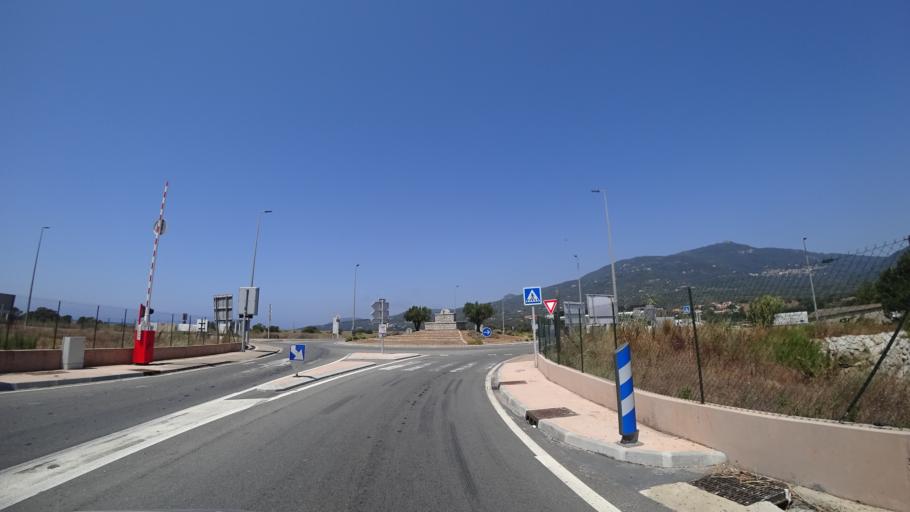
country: FR
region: Corsica
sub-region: Departement de la Corse-du-Sud
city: Propriano
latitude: 41.6840
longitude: 8.9217
